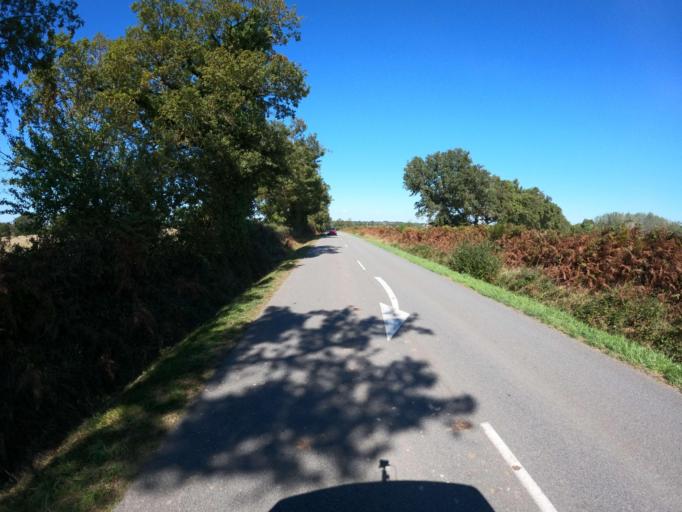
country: FR
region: Limousin
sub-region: Departement de la Haute-Vienne
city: Le Dorat
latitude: 46.2482
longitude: 1.0476
